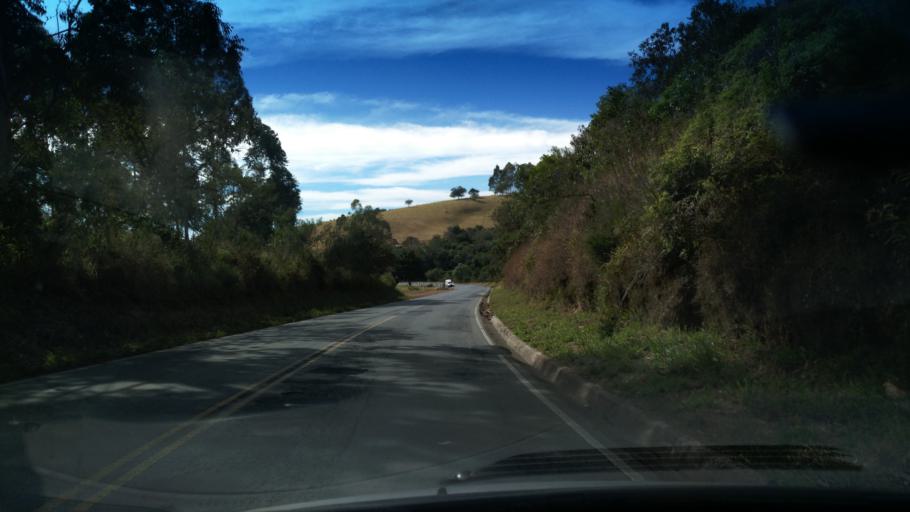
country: BR
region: Minas Gerais
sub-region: Andradas
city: Andradas
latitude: -22.0424
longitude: -46.3539
